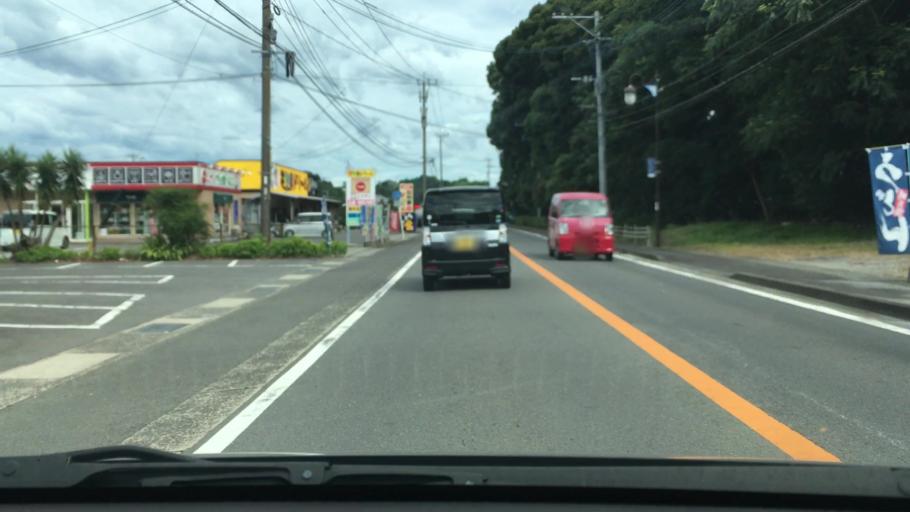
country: JP
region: Nagasaki
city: Togitsu
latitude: 32.8878
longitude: 129.7881
